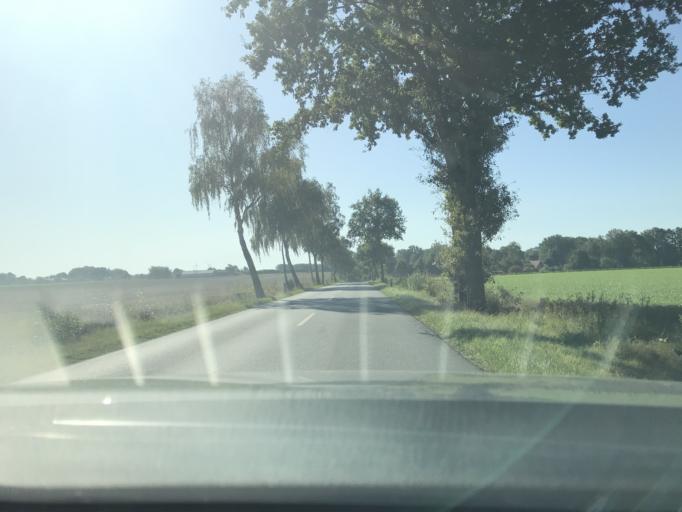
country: DE
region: Lower Saxony
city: Schwienau
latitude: 52.9848
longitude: 10.4450
